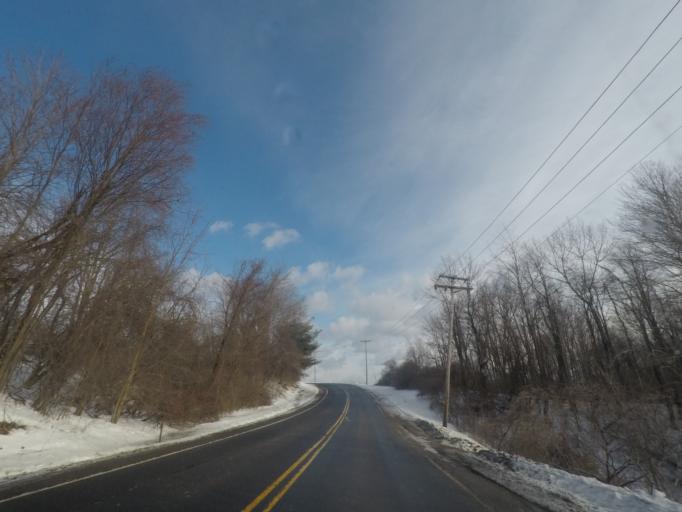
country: US
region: New York
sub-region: Saratoga County
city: Mechanicville
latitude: 42.8504
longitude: -73.7047
